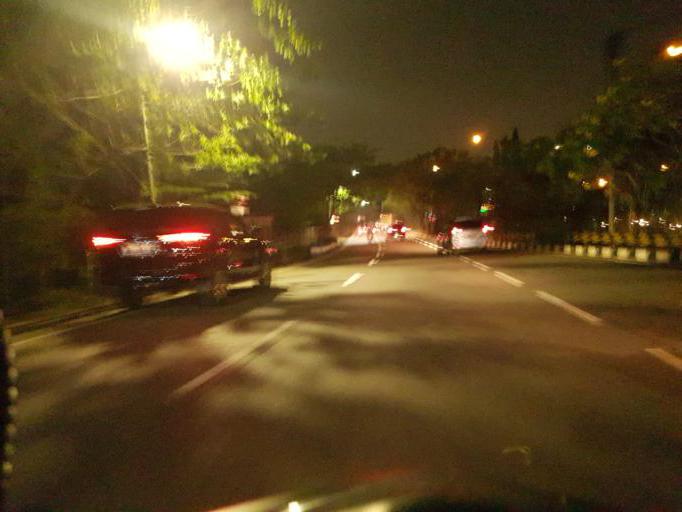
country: ID
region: West Java
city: Cileungsir
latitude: -6.3117
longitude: 106.9026
